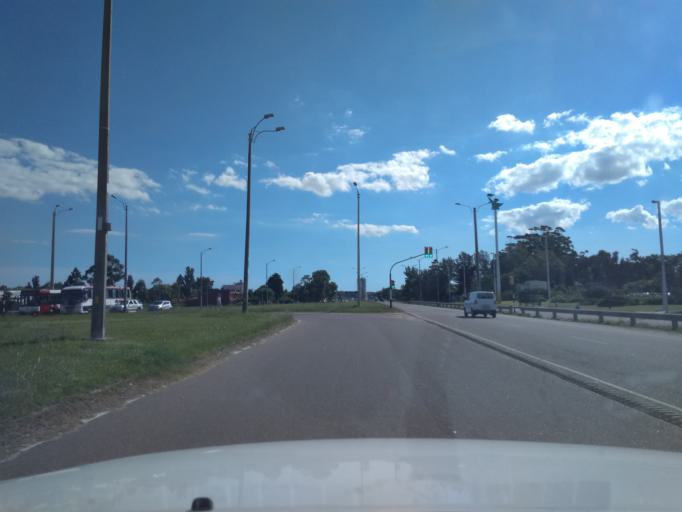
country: UY
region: Canelones
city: Barra de Carrasco
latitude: -34.8669
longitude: -56.0219
